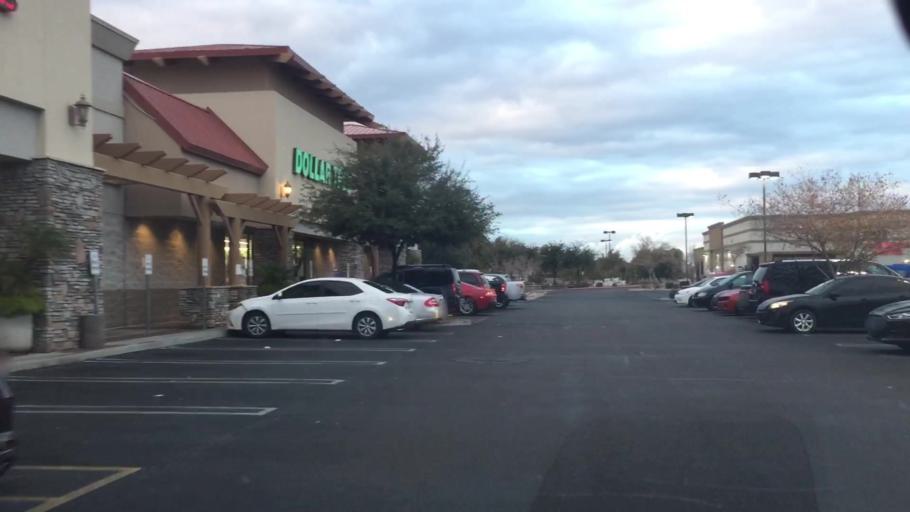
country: US
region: Arizona
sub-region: Maricopa County
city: Laveen
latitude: 33.3784
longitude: -112.1735
